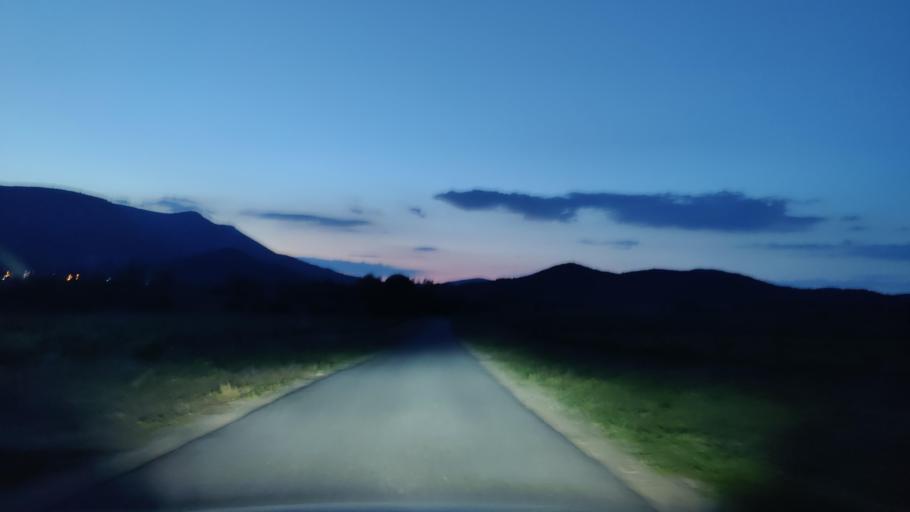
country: FR
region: Languedoc-Roussillon
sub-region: Departement des Pyrenees-Orientales
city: Estagel
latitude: 42.8831
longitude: 2.7360
